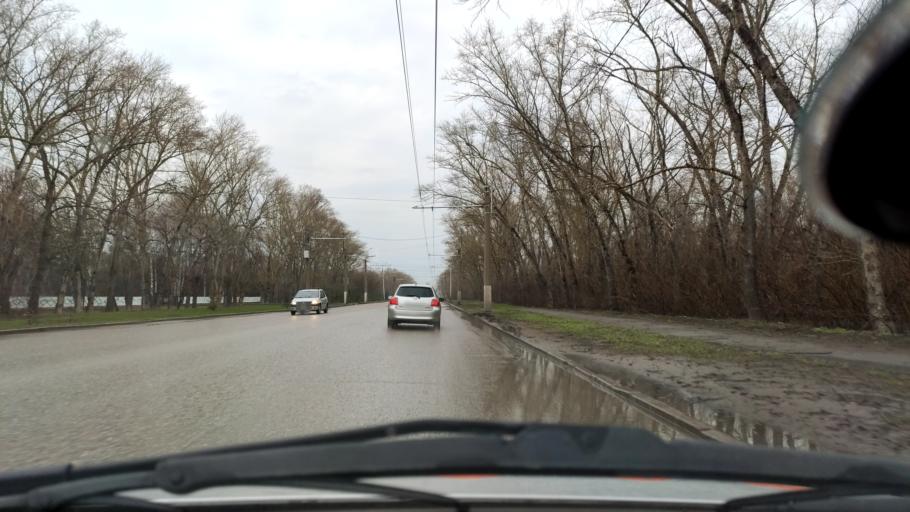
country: RU
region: Bashkortostan
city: Sterlitamak
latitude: 53.6572
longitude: 55.9487
